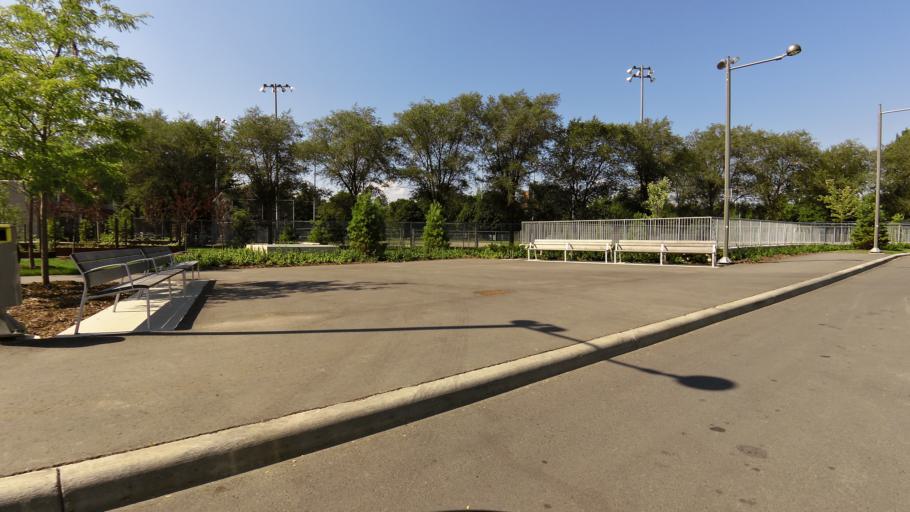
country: CA
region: Ontario
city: Ottawa
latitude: 45.4011
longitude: -75.6818
